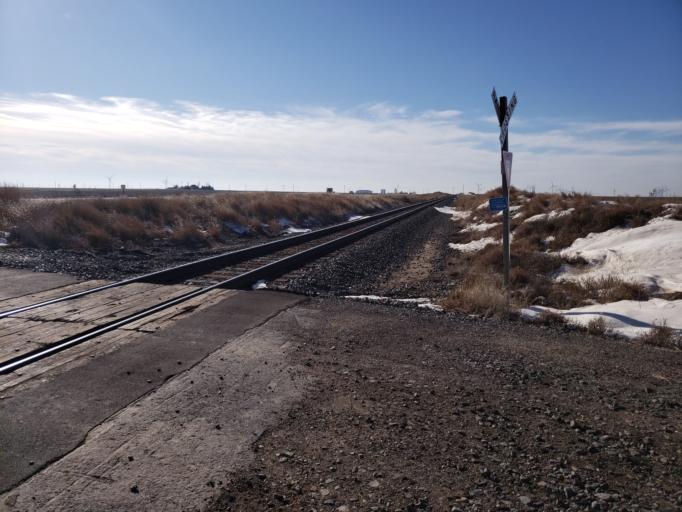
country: US
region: Kansas
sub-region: Ford County
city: Dodge City
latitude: 37.5033
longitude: -99.8505
